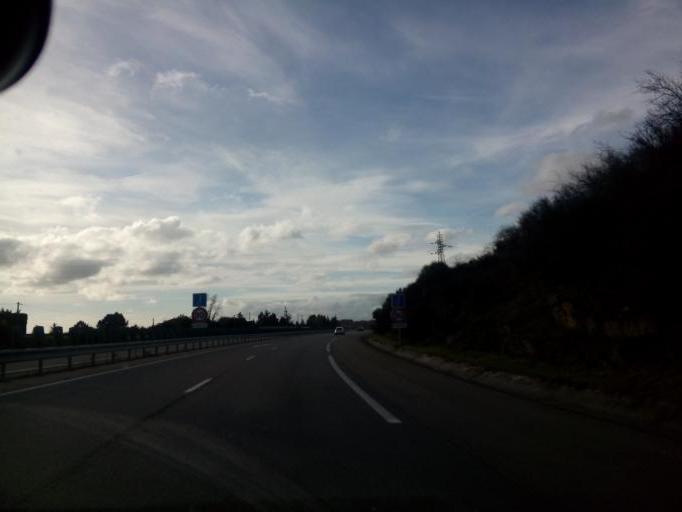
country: FR
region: Rhone-Alpes
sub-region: Departement de l'Ardeche
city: Peaugres
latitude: 45.2955
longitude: 4.7366
